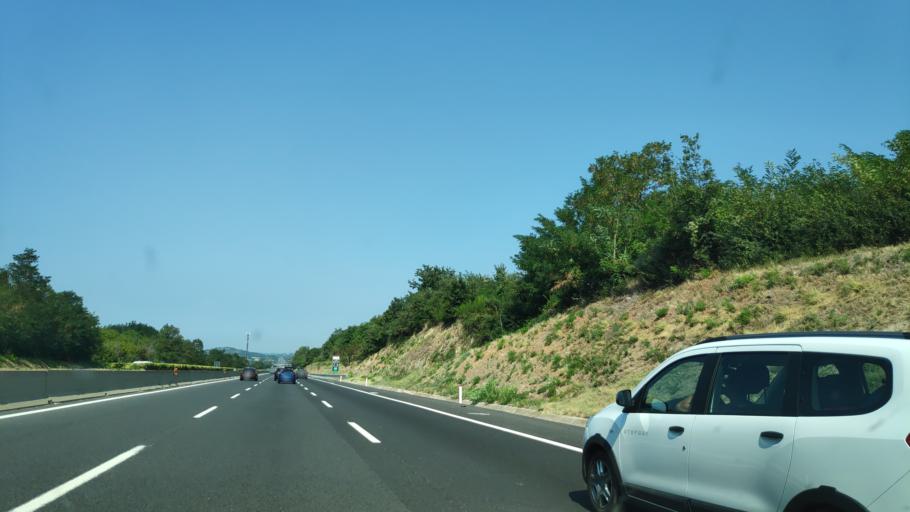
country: IT
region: Campania
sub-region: Provincia di Caserta
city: San Pietro Infine
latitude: 41.4143
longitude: 13.9455
